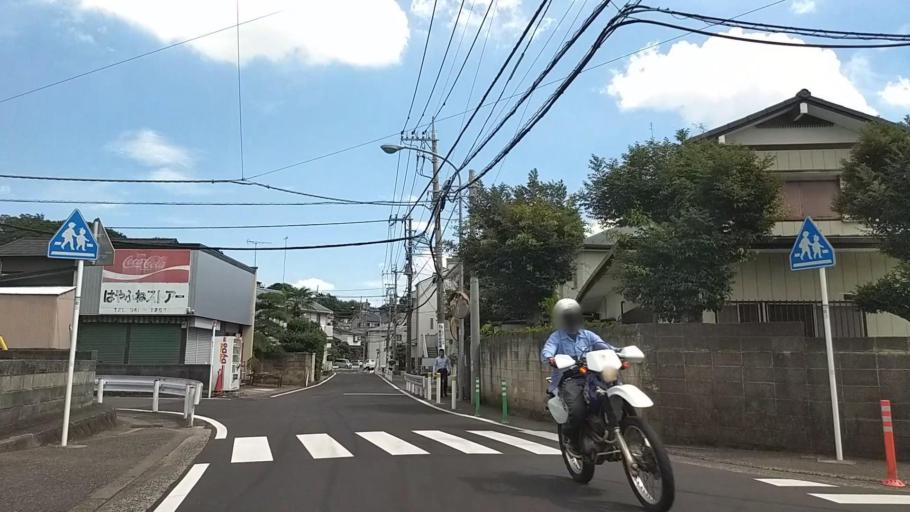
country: JP
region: Kanagawa
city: Yokohama
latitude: 35.5221
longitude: 139.5740
